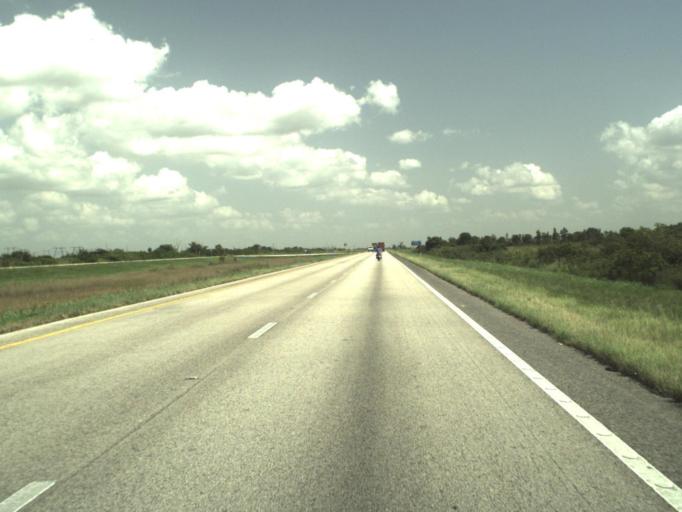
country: US
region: Florida
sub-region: Broward County
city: Weston
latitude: 26.0922
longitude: -80.4340
